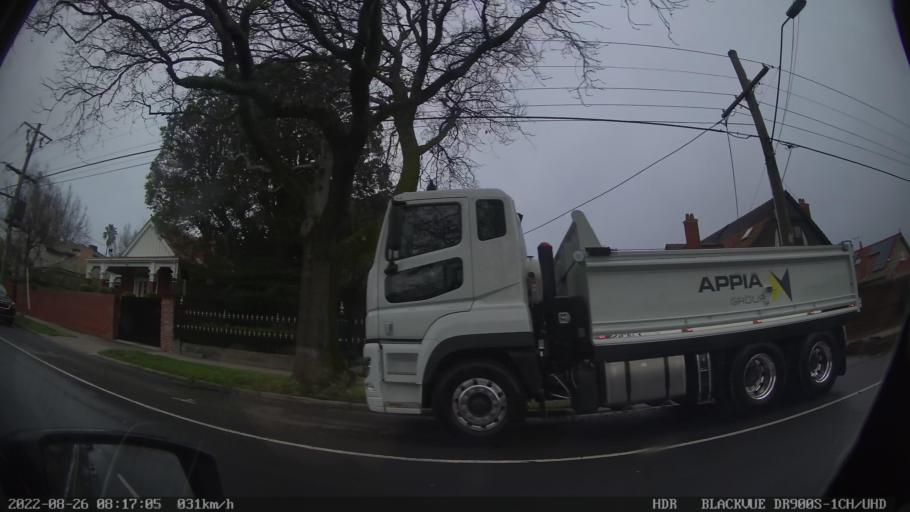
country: AU
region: Victoria
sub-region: Glen Eira
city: Elsternwick
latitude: -37.8896
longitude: 145.0054
